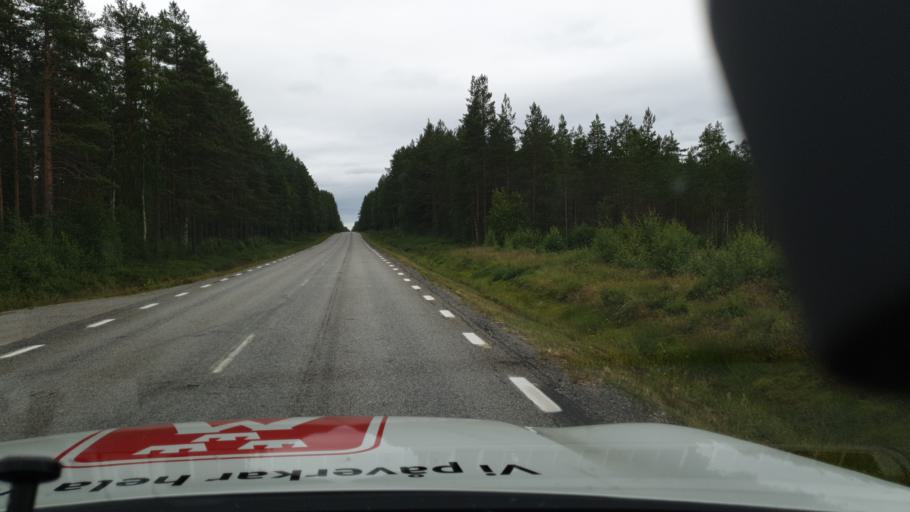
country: SE
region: Vaesterbotten
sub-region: Umea Kommun
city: Saevar
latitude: 64.0495
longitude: 20.4851
